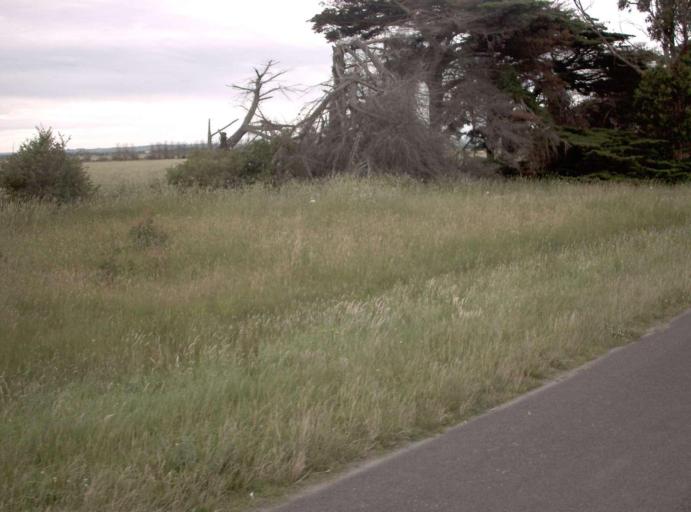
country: AU
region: Victoria
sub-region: Cardinia
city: Koo-Wee-Rup
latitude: -38.2260
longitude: 145.5098
